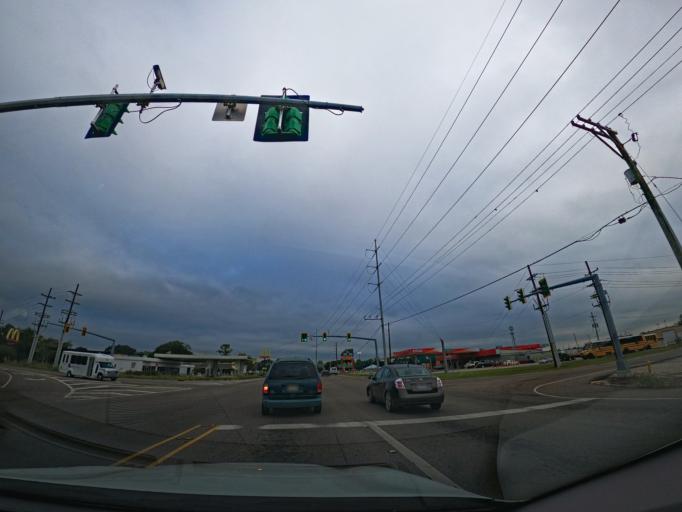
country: US
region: Louisiana
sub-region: Terrebonne Parish
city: Presquille
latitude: 29.5705
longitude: -90.6829
